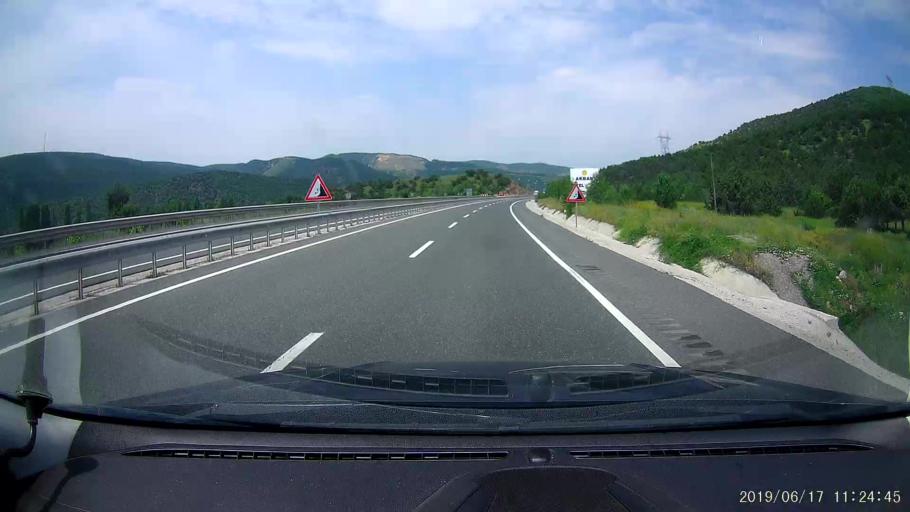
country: TR
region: Cankiri
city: Ilgaz
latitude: 40.8854
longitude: 33.6956
